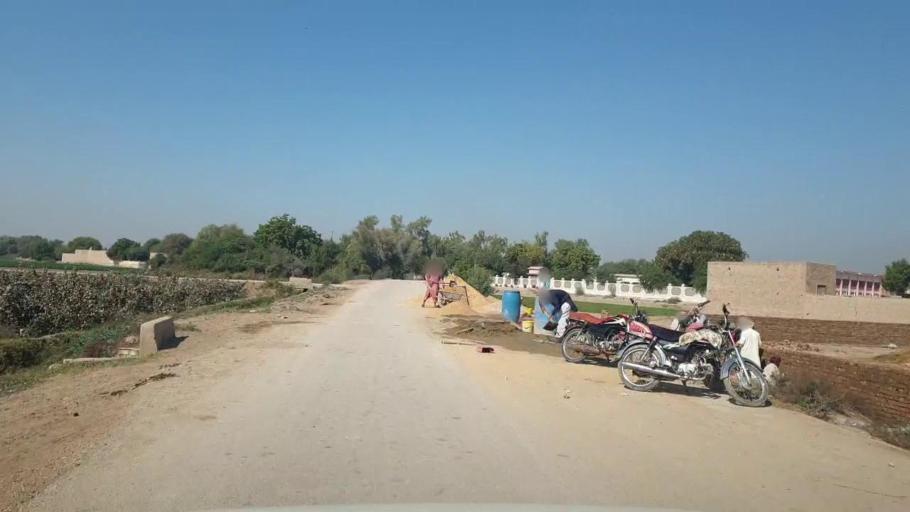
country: PK
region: Sindh
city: Bhan
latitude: 26.6481
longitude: 67.7149
